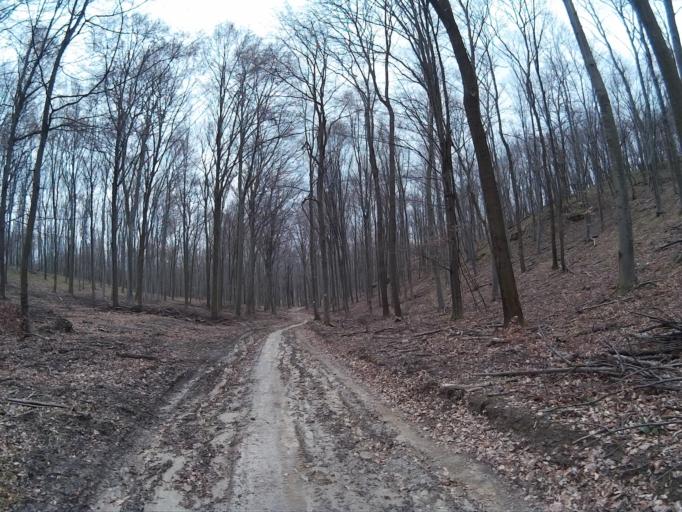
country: HU
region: Veszprem
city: Zirc
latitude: 47.1814
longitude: 17.8771
